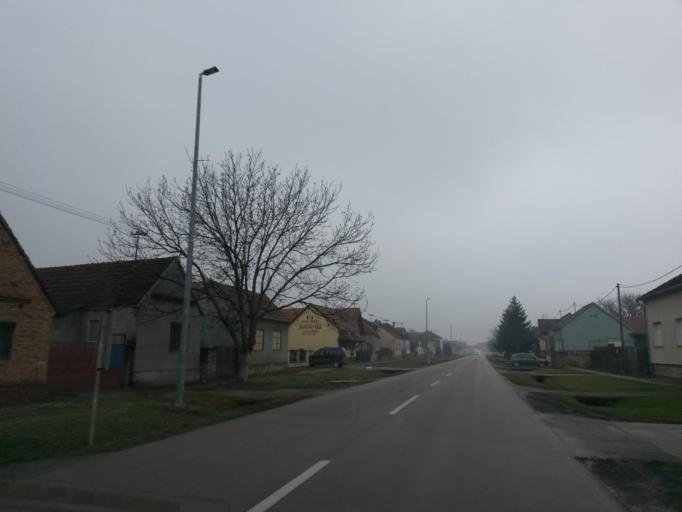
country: HR
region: Vukovarsko-Srijemska
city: Andrijasevci
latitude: 45.2195
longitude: 18.7306
